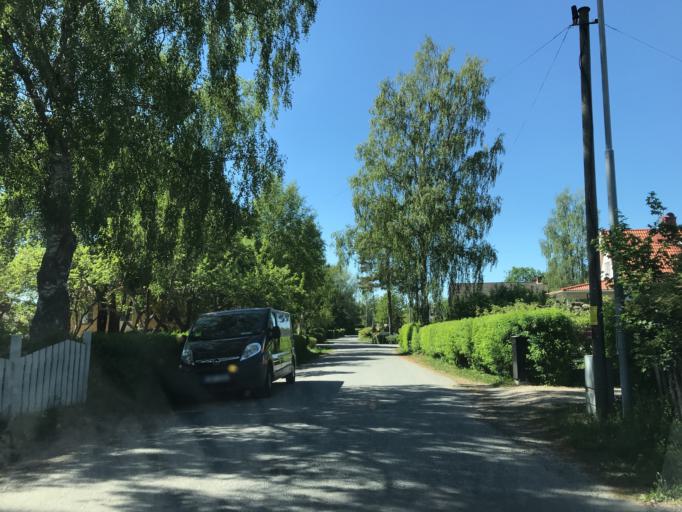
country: SE
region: Stockholm
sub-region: Sollentuna Kommun
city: Sollentuna
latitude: 59.4188
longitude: 17.9682
